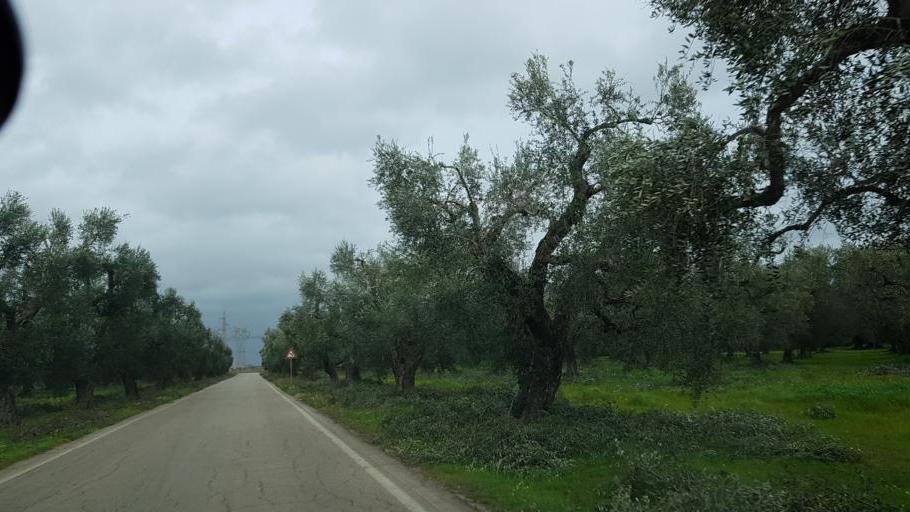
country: IT
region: Apulia
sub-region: Provincia di Brindisi
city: Brindisi
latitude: 40.5973
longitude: 17.8992
